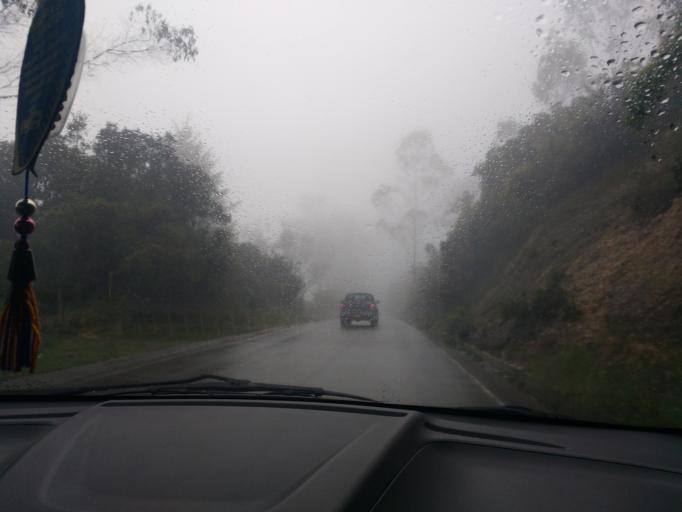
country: CO
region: Bogota D.C.
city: Bogota
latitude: 4.5913
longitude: -74.0277
